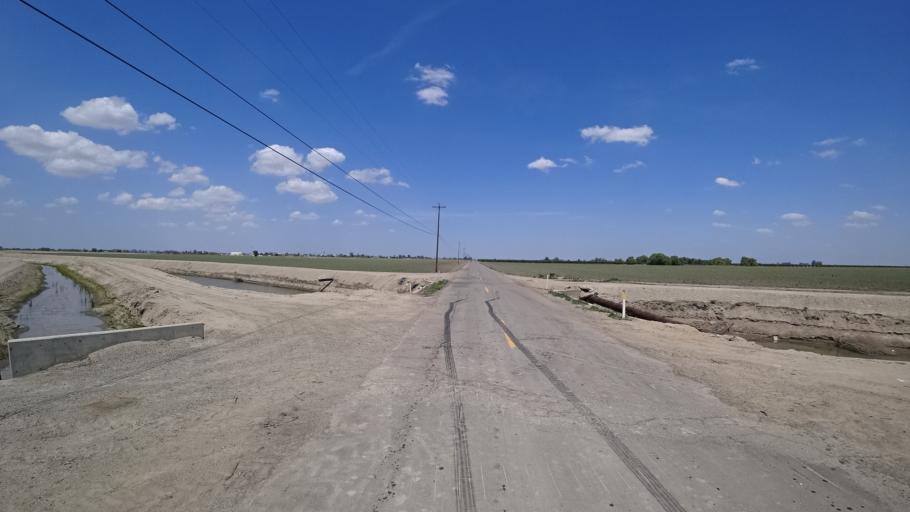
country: US
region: California
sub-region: Kings County
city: Stratford
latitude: 36.1721
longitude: -119.8161
